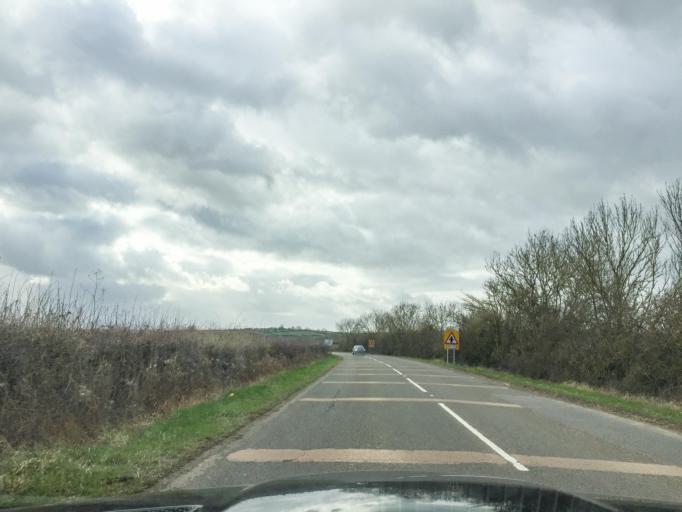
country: GB
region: England
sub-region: Warwickshire
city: Shipston on Stour
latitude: 52.0597
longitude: -1.6058
